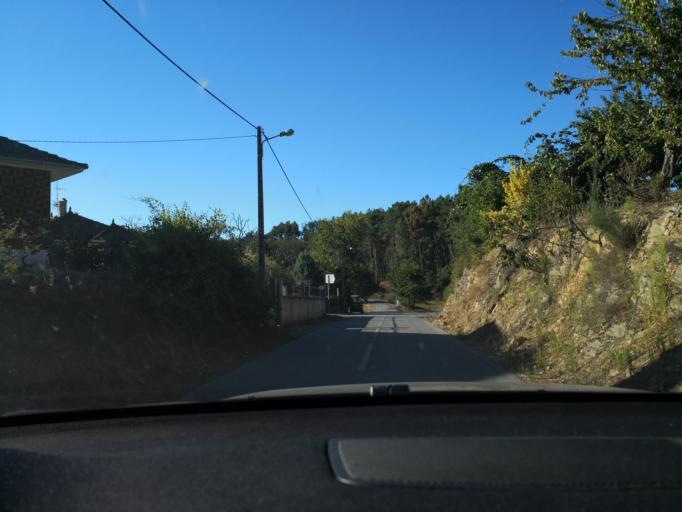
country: PT
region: Vila Real
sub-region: Sabrosa
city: Vilela
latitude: 41.2394
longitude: -7.6132
